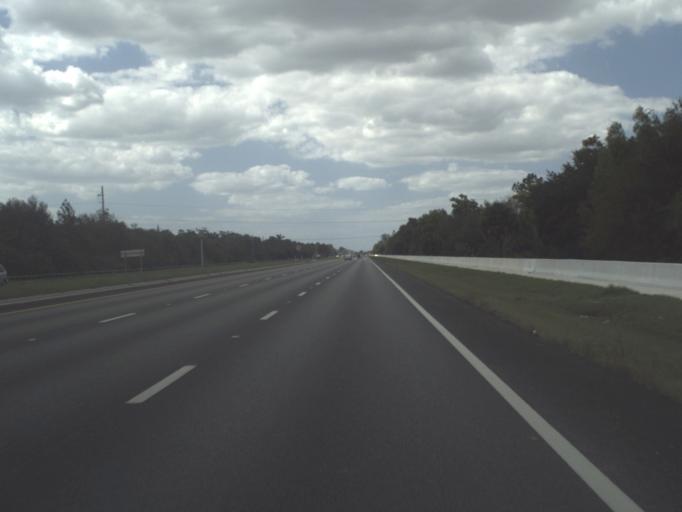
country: US
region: Florida
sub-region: Collier County
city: Lely Resort
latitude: 26.0514
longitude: -81.6805
